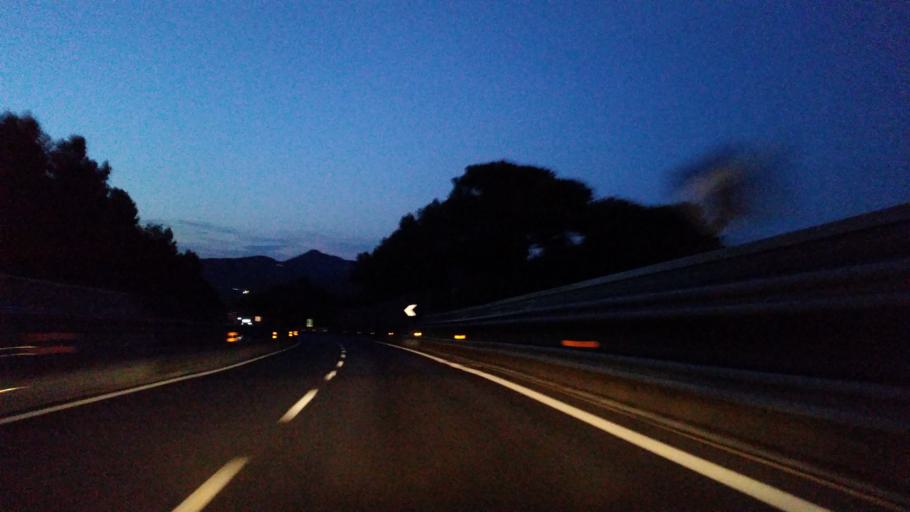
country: IT
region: Liguria
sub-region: Provincia di Savona
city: Andora
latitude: 43.9536
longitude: 8.1346
